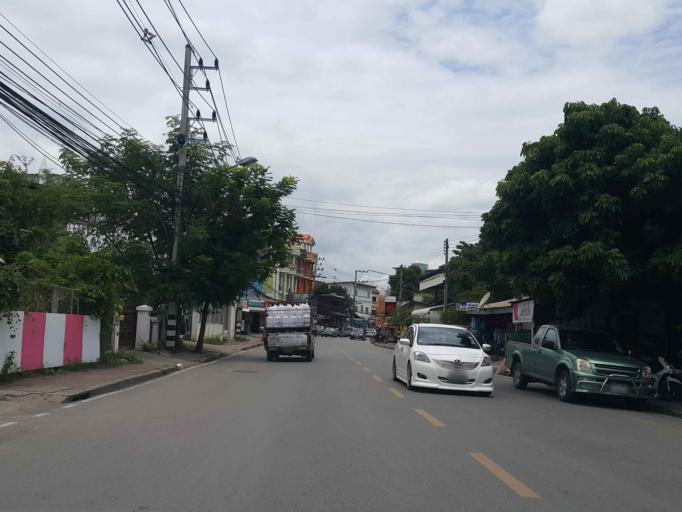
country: TH
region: Chiang Mai
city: Chiang Mai
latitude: 18.7675
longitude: 99.0015
